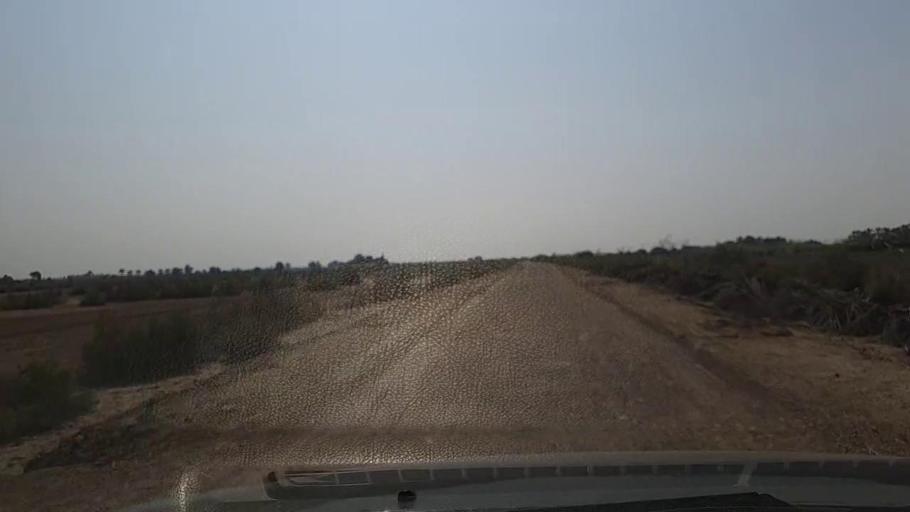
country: PK
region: Sindh
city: Mirpur Sakro
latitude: 24.3852
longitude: 67.6632
